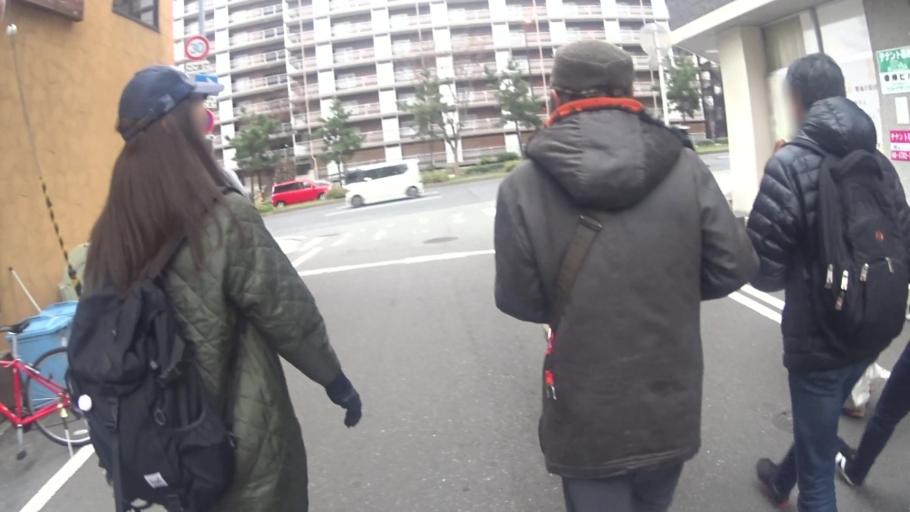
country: JP
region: Osaka
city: Osaka-shi
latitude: 34.6663
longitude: 135.5266
